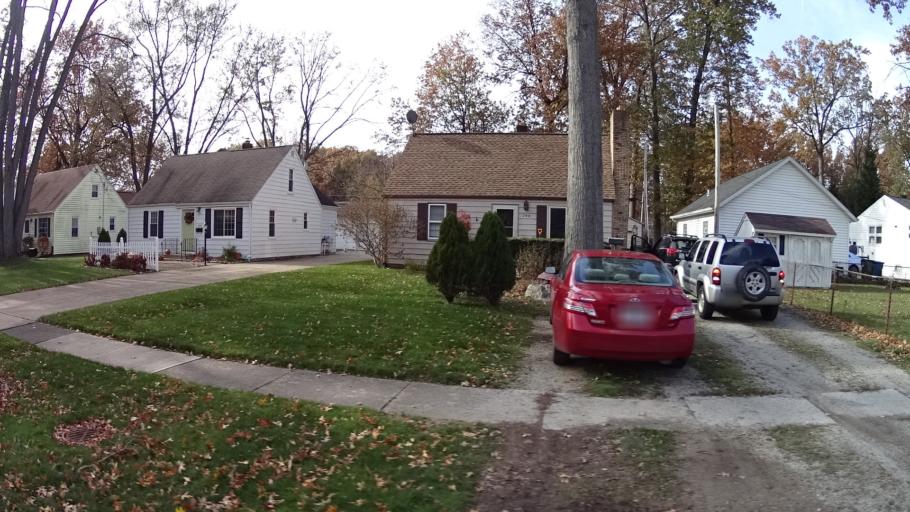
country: US
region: Ohio
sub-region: Lorain County
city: Avon Lake
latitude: 41.5014
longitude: -82.0251
